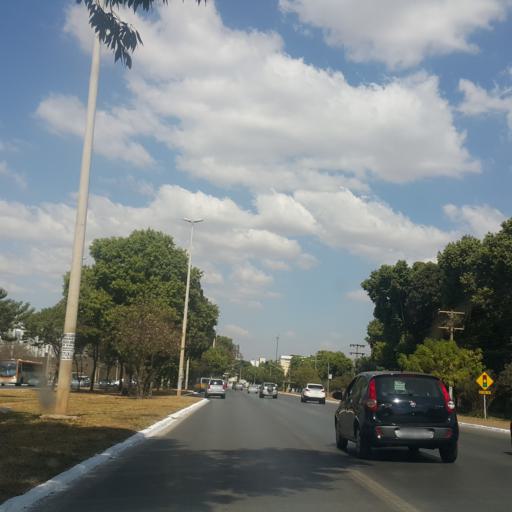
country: BR
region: Federal District
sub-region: Brasilia
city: Brasilia
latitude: -15.8183
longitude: -48.0576
